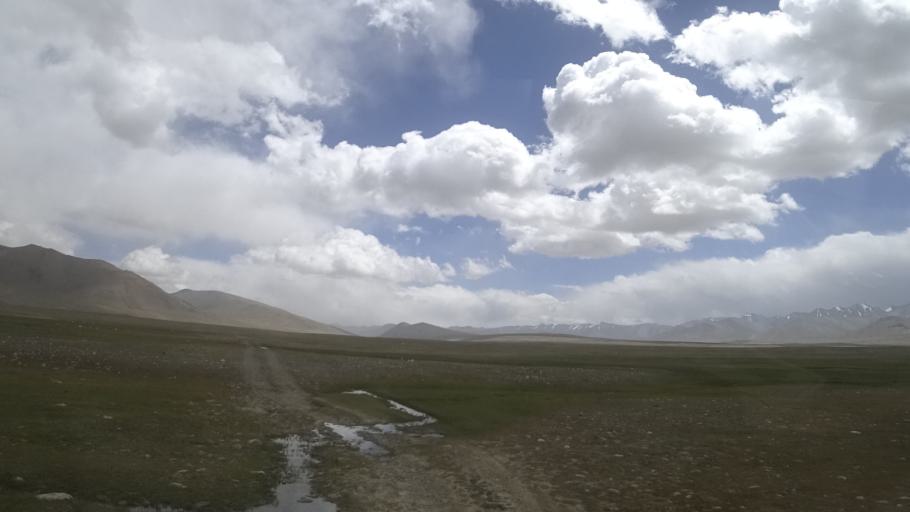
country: TJ
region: Gorno-Badakhshan
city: Murghob
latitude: 37.4885
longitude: 73.9969
